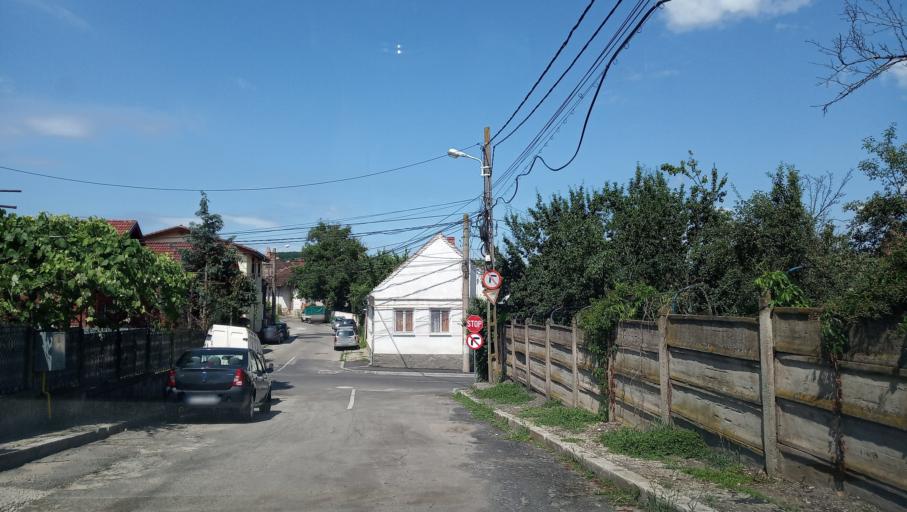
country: RO
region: Hunedoara
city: Hunedoara
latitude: 45.7489
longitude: 22.8965
